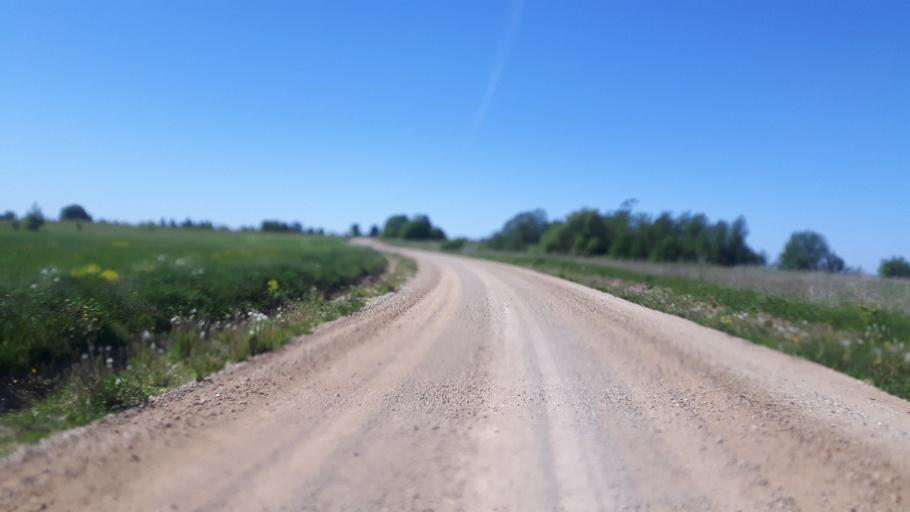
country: EE
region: Ida-Virumaa
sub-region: Toila vald
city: Voka
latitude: 59.4141
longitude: 27.6306
